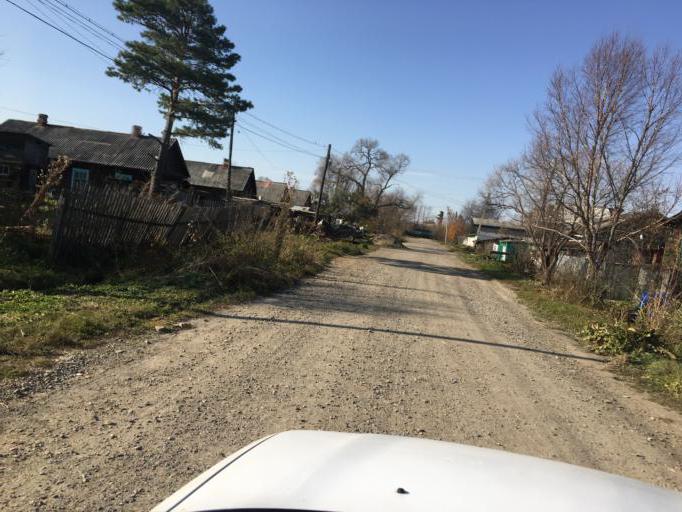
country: RU
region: Primorskiy
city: Dal'nerechensk
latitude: 45.9197
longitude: 133.7222
